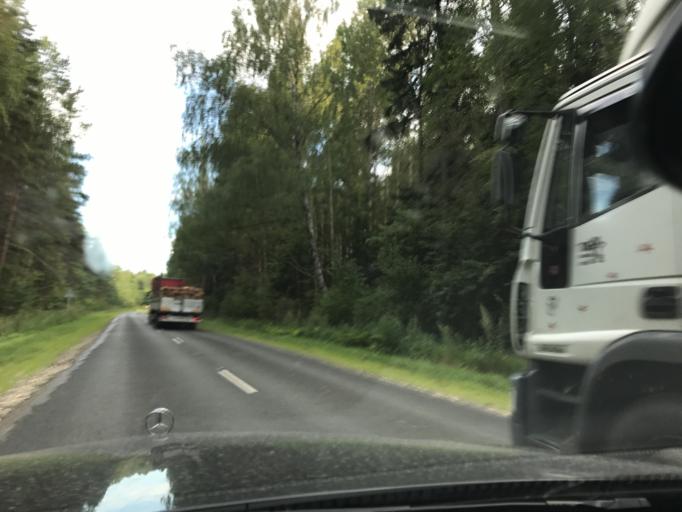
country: RU
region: Vladimir
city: Raduzhnyy
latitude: 55.9931
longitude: 40.2726
